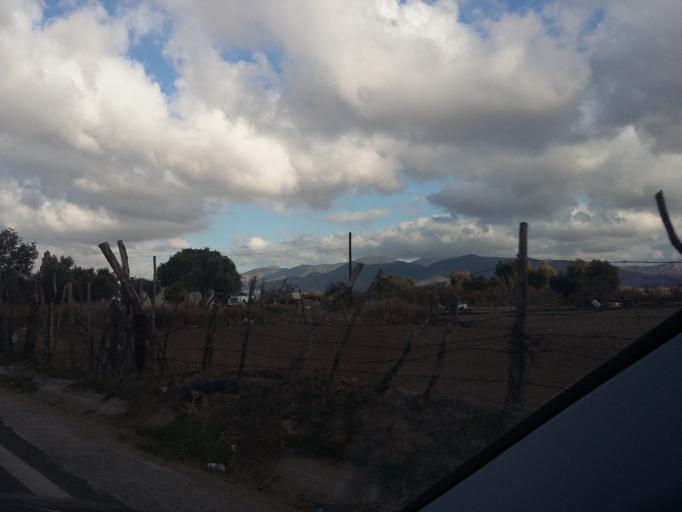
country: MX
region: Baja California
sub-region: Ensenada
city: Rancho Verde
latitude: 32.0651
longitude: -116.6413
